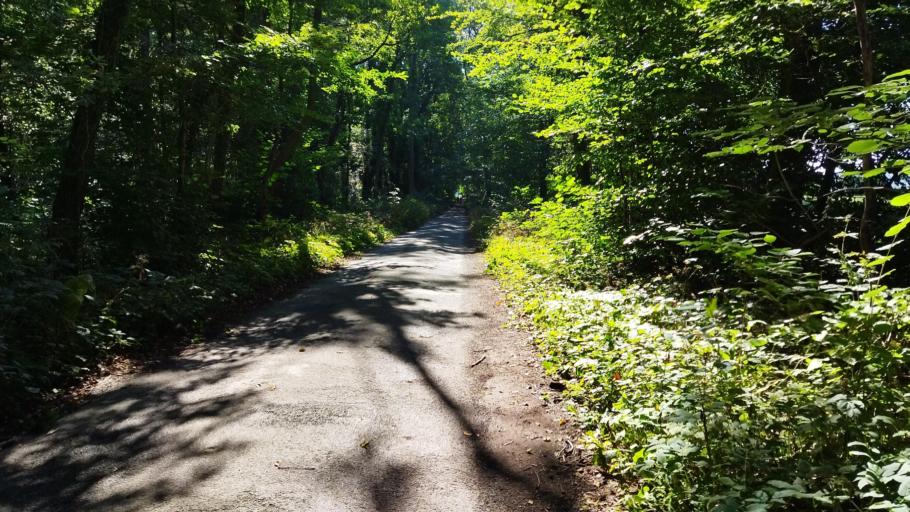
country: DE
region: Lower Saxony
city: Laar
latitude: 52.3758
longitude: 8.2372
